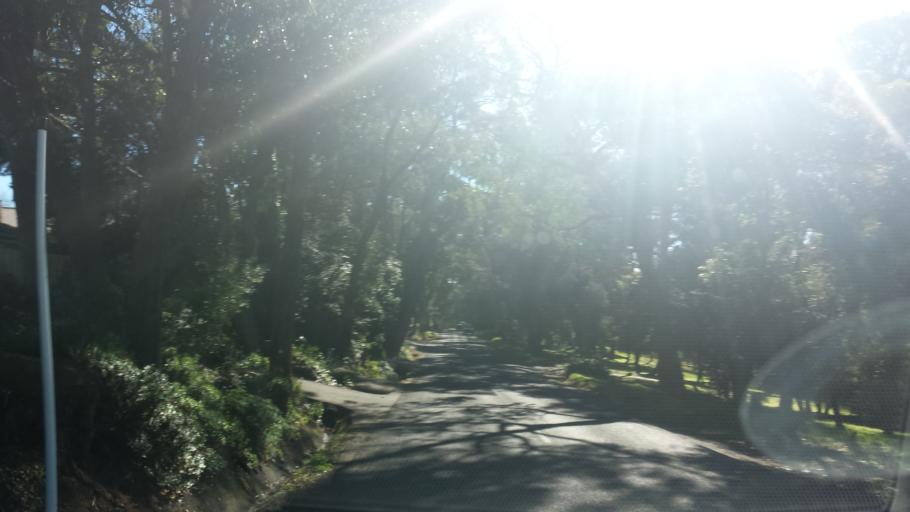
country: AU
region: Victoria
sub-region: Yarra Ranges
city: Lilydale
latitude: -37.7604
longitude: 145.3718
